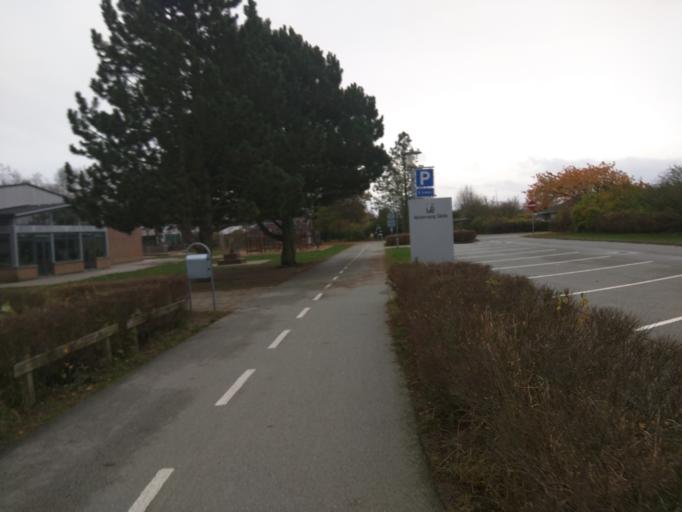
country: DK
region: Central Jutland
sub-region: Viborg Kommune
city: Viborg
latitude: 56.4653
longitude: 9.3881
